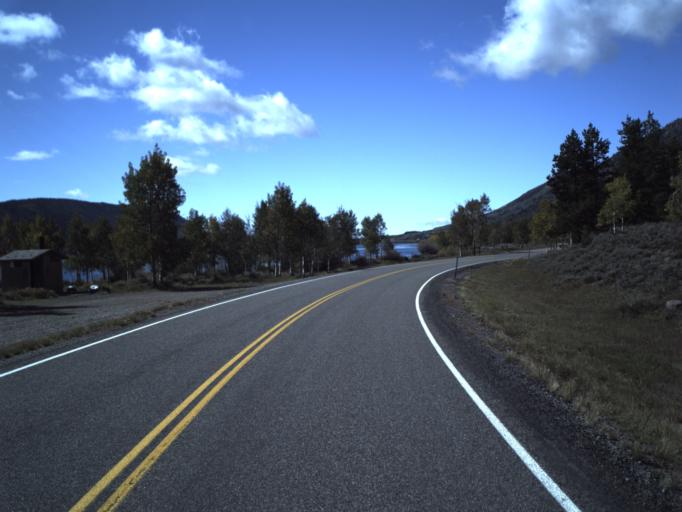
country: US
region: Utah
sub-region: Wayne County
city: Loa
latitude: 38.5596
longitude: -111.7089
